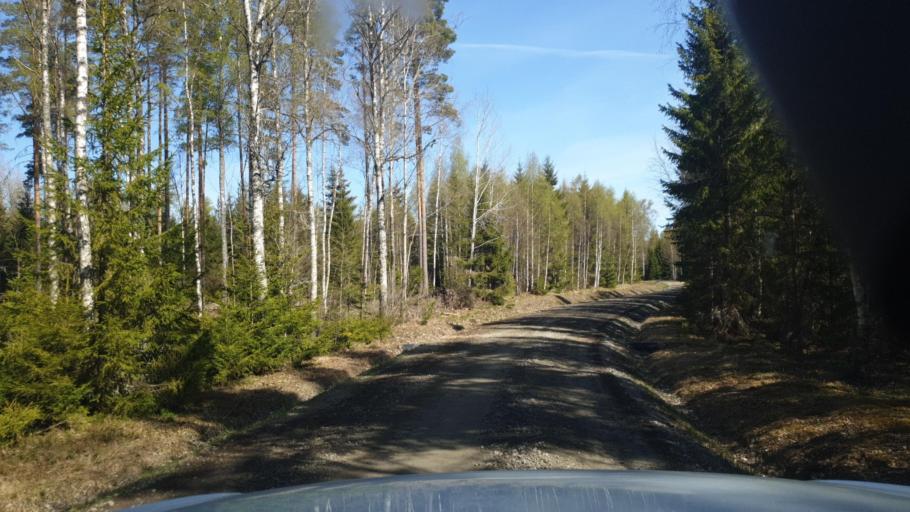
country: SE
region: Vaermland
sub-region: Karlstads Kommun
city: Edsvalla
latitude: 59.4648
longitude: 13.1214
